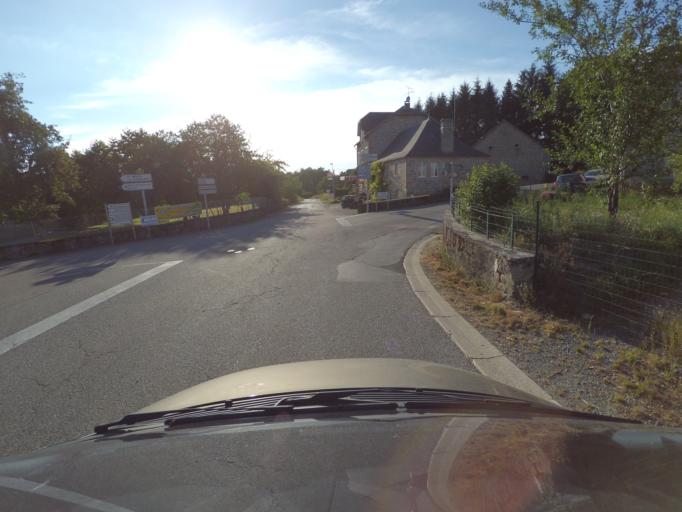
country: FR
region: Limousin
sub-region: Departement de la Correze
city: Bugeat
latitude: 45.7065
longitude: 2.0475
